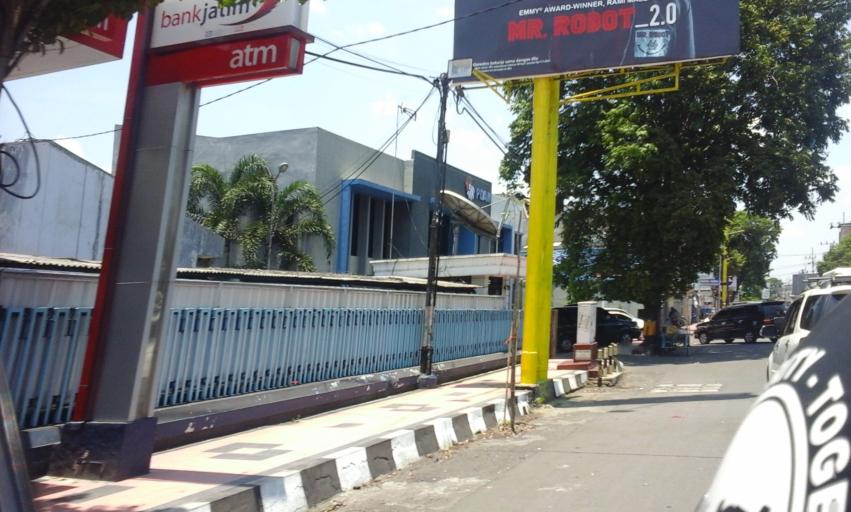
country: ID
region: East Java
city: Kepatihan
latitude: -8.1754
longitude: 113.7005
